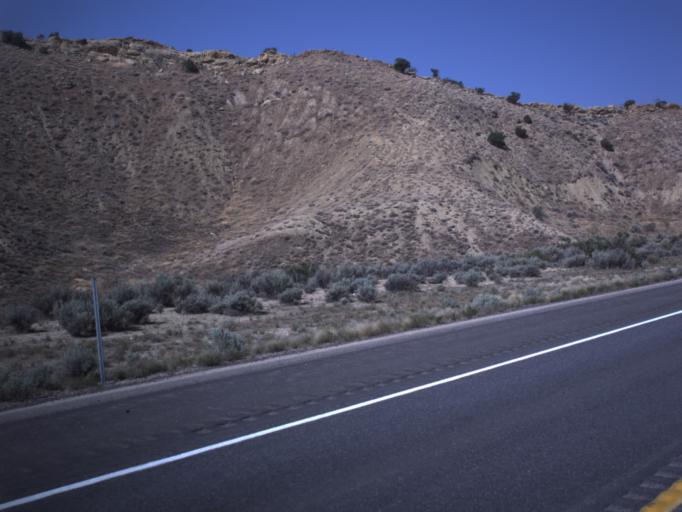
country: US
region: Colorado
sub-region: Rio Blanco County
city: Rangely
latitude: 40.2788
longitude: -109.0611
